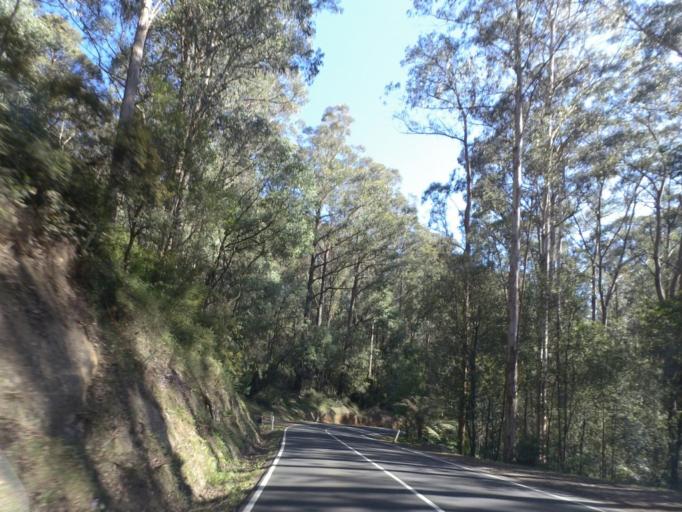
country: AU
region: Victoria
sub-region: Yarra Ranges
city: Millgrove
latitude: -37.8772
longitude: 145.7853
